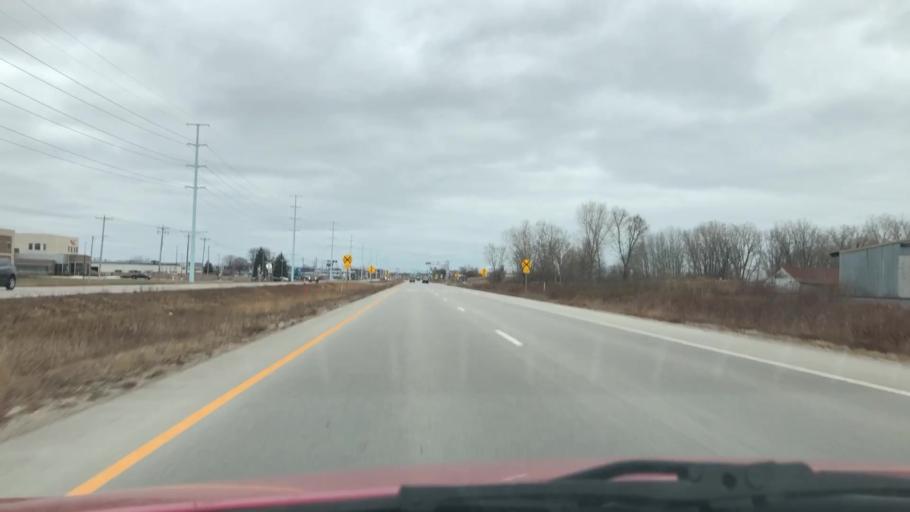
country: US
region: Wisconsin
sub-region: Brown County
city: Ashwaubenon
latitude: 44.4683
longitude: -88.0673
